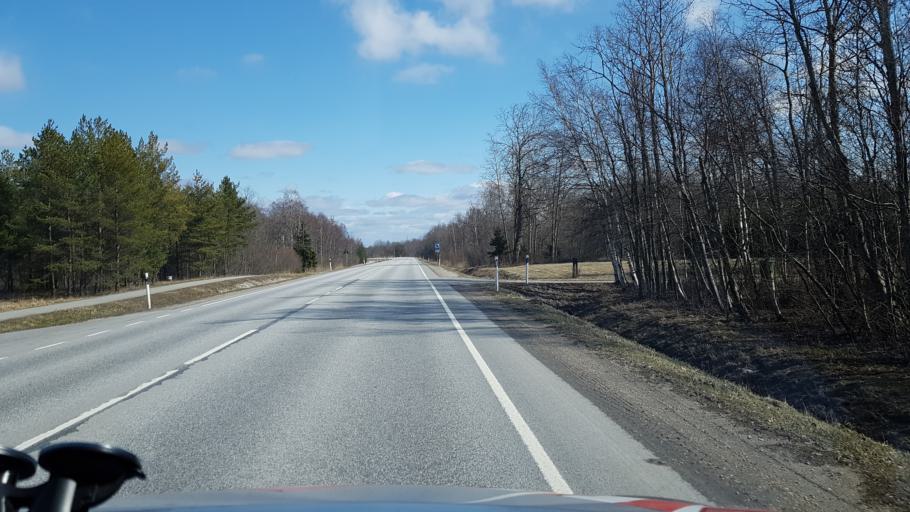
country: EE
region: Laeaene
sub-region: Ridala Parish
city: Uuemoisa
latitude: 58.9490
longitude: 23.6437
